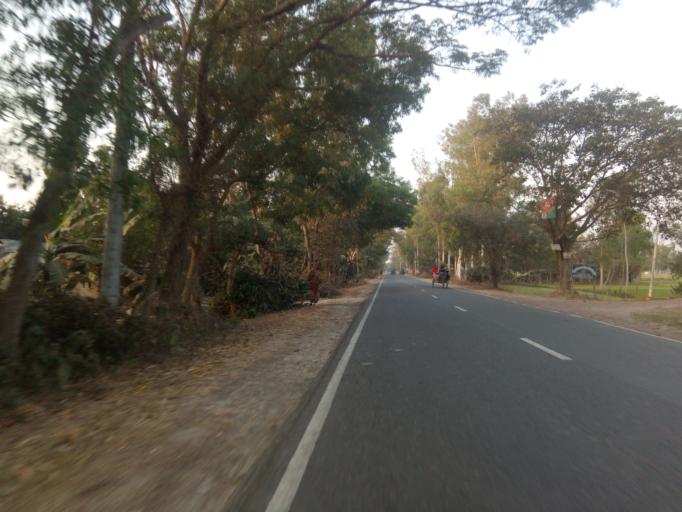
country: BD
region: Rajshahi
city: Bogra
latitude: 24.6184
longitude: 89.2411
